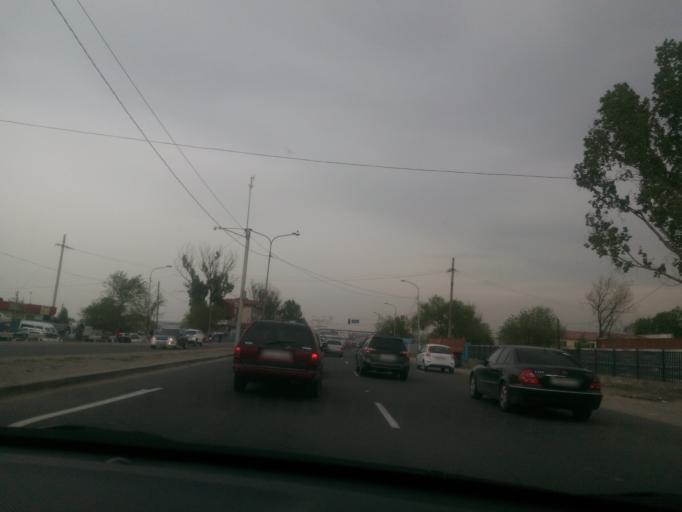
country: KZ
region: Almaty Oblysy
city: Burunday
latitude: 43.2298
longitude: 76.7677
